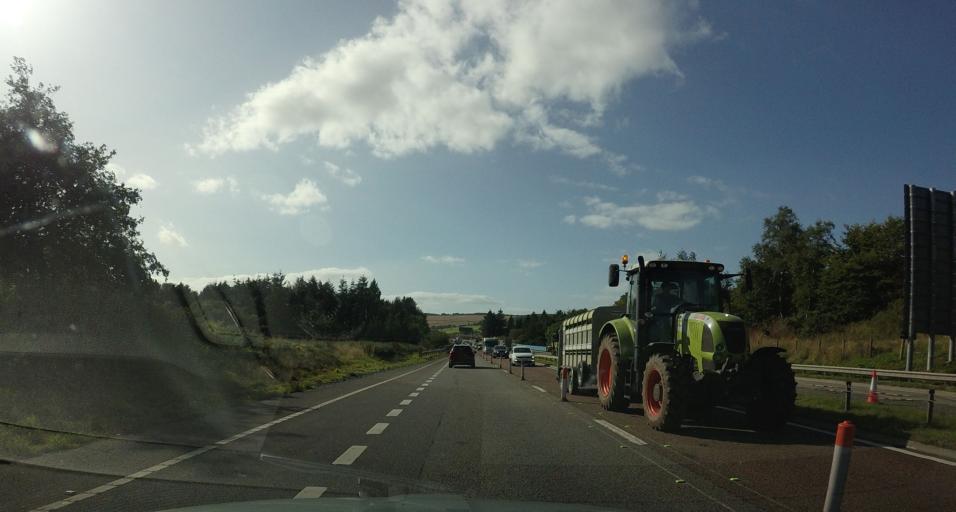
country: GB
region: Scotland
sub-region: Aberdeenshire
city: Stonehaven
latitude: 56.9758
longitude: -2.2201
